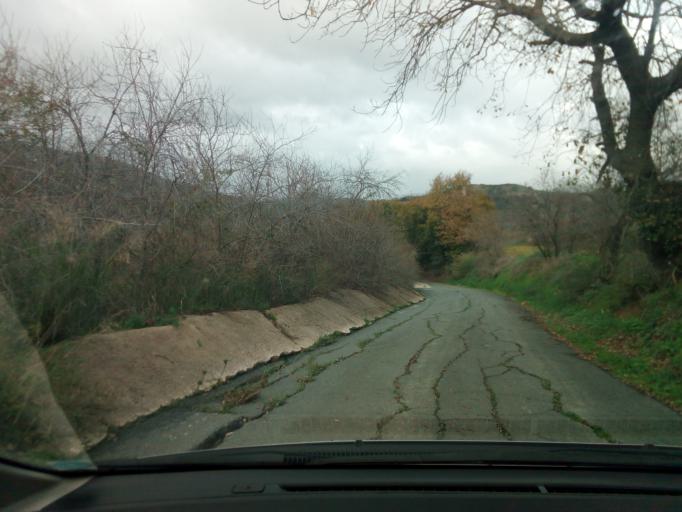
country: CY
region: Pafos
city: Tala
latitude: 34.9299
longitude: 32.4709
